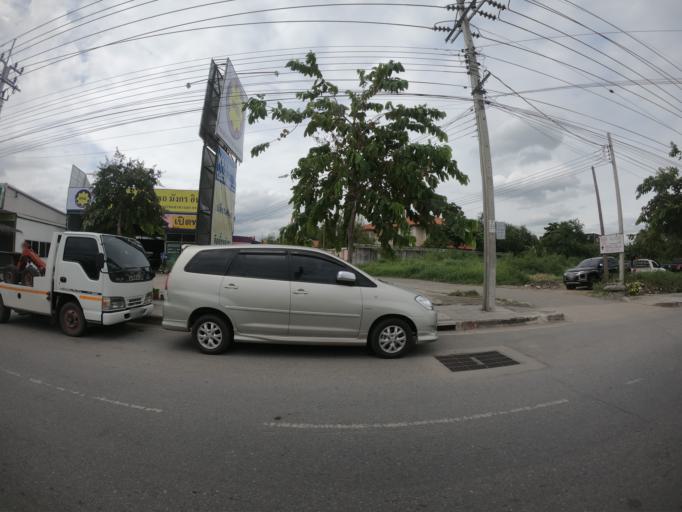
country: TH
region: Bangkok
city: Bang Na
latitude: 13.6834
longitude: 100.6700
